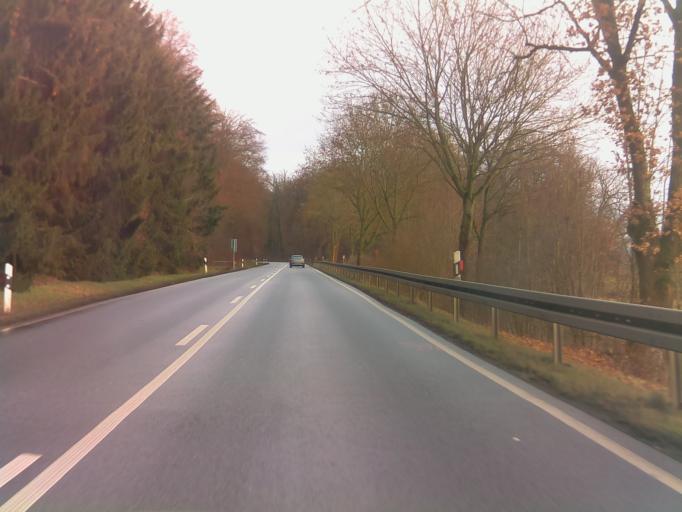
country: DE
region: Hesse
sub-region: Regierungsbezirk Giessen
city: Lich
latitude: 50.5299
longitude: 8.8535
